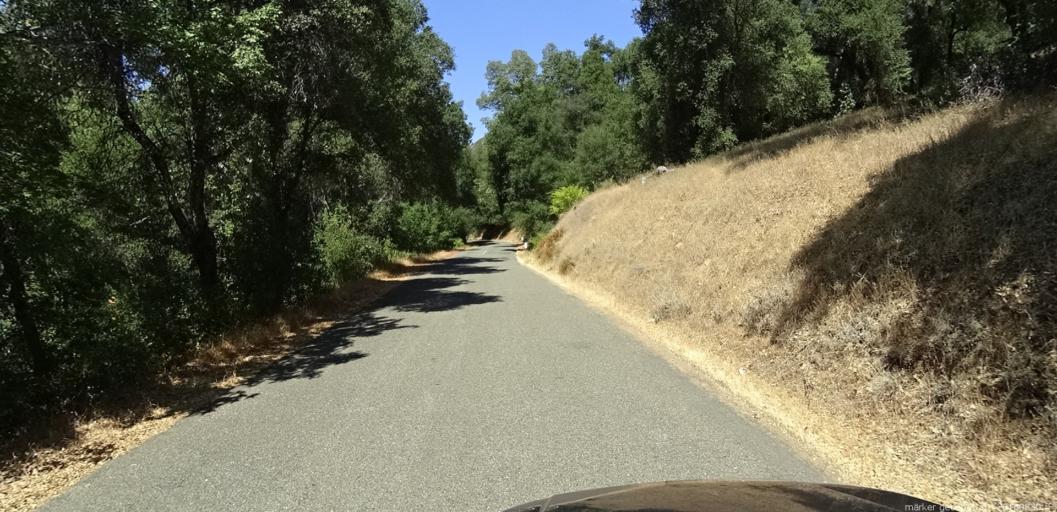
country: US
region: California
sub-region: Monterey County
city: King City
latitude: 36.0094
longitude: -121.4053
